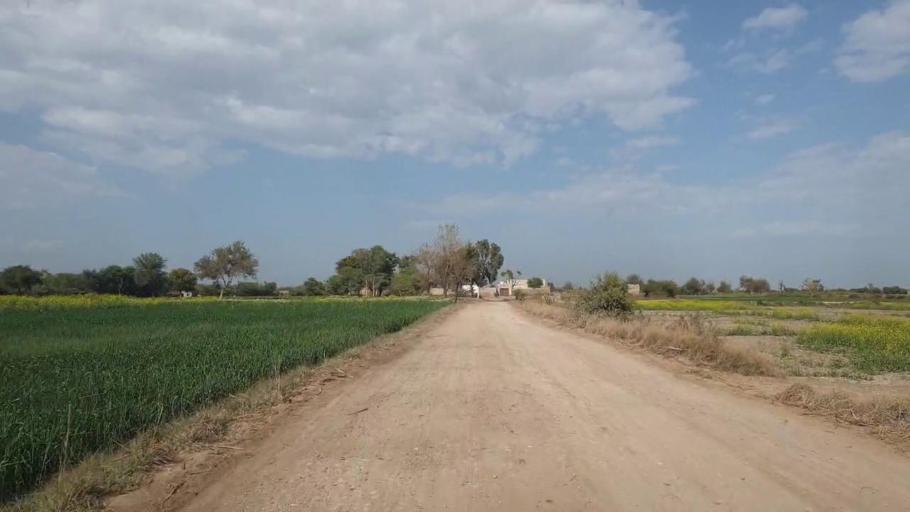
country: PK
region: Sindh
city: Shahdadpur
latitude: 25.9822
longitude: 68.4775
